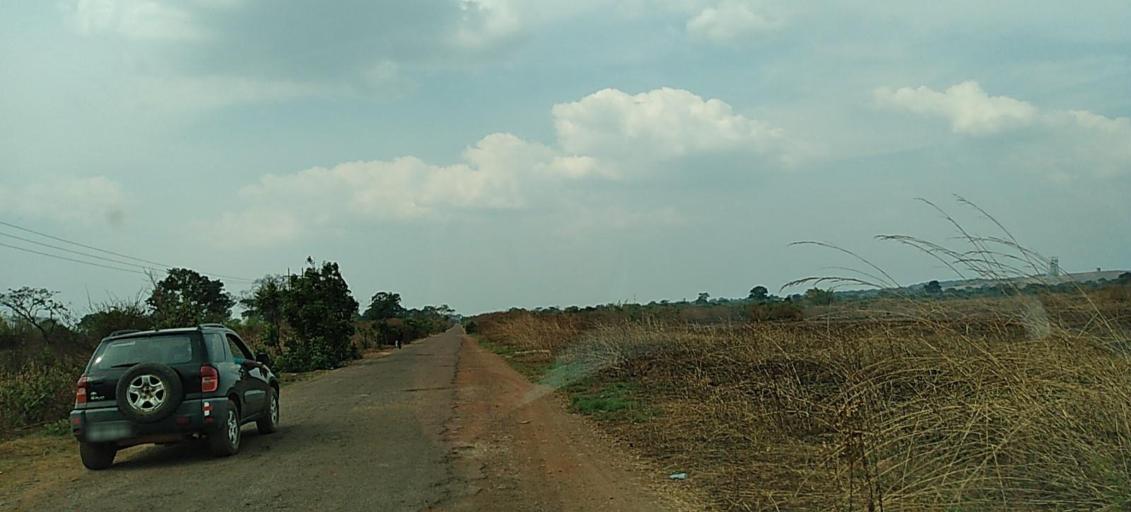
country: ZM
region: Copperbelt
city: Chililabombwe
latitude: -12.3915
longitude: 27.8068
